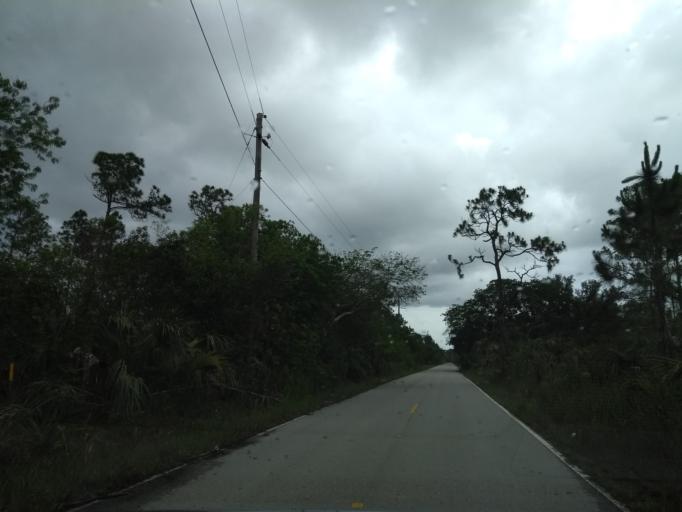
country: US
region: Florida
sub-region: Miami-Dade County
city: The Hammocks
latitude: 25.7513
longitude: -80.9350
